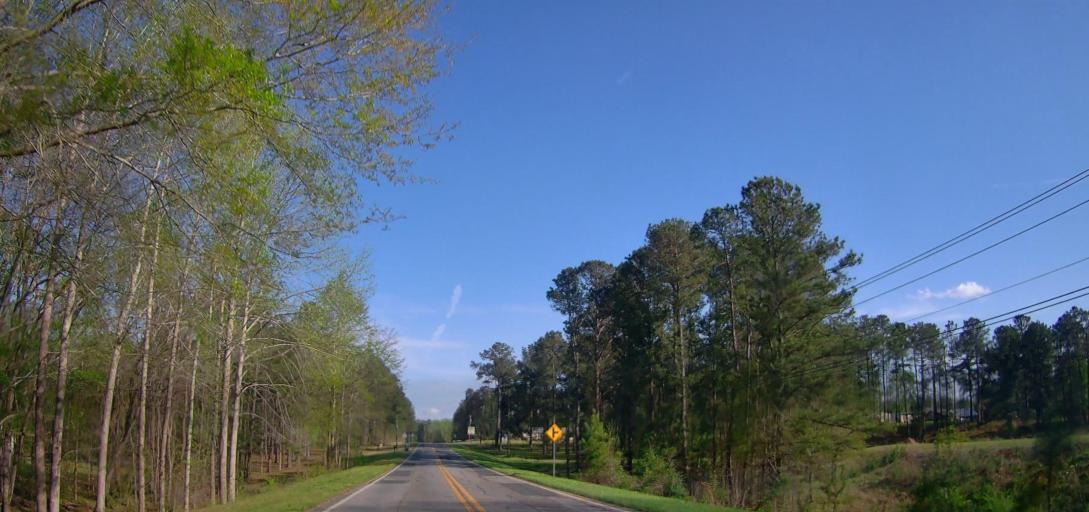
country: US
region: Georgia
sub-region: Baldwin County
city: Milledgeville
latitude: 33.1482
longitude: -83.2571
